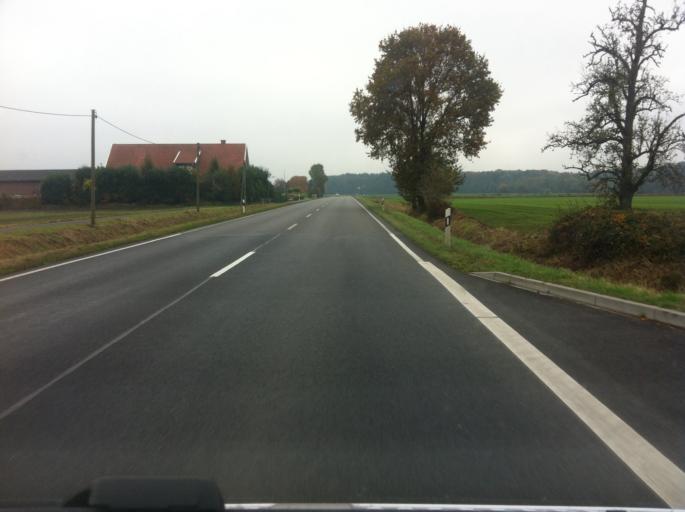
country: DE
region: North Rhine-Westphalia
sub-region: Regierungsbezirk Munster
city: Sudlohn
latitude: 51.9482
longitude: 6.8194
